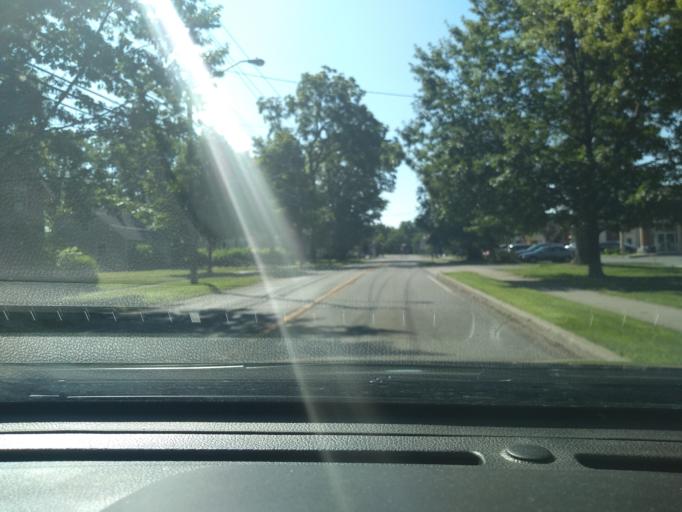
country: US
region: New York
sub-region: Erie County
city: Billington Heights
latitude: 42.7691
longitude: -78.6306
